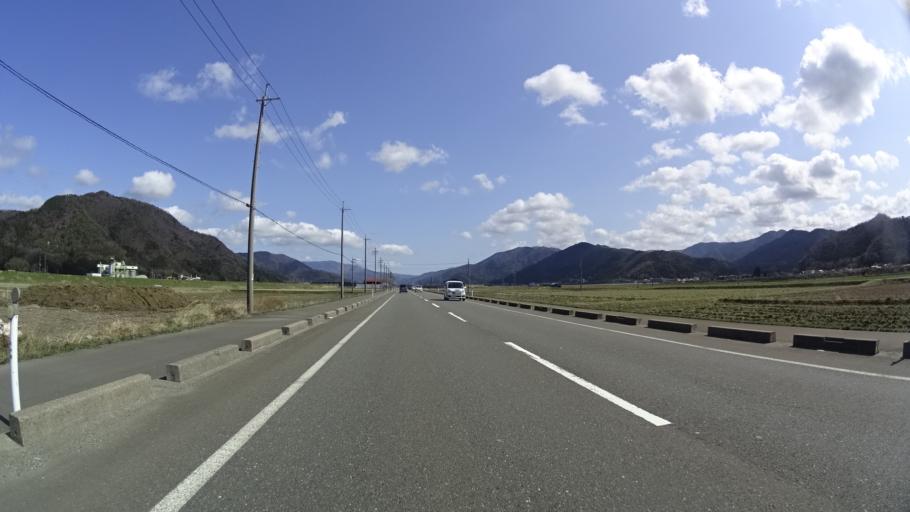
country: JP
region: Fukui
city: Obama
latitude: 35.4866
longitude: 135.7895
